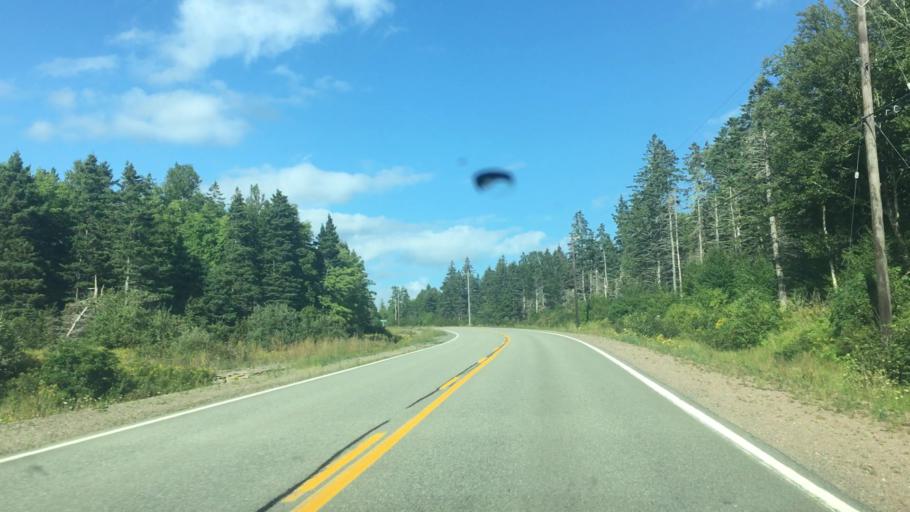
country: CA
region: Nova Scotia
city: Sydney
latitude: 45.8537
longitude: -60.6318
